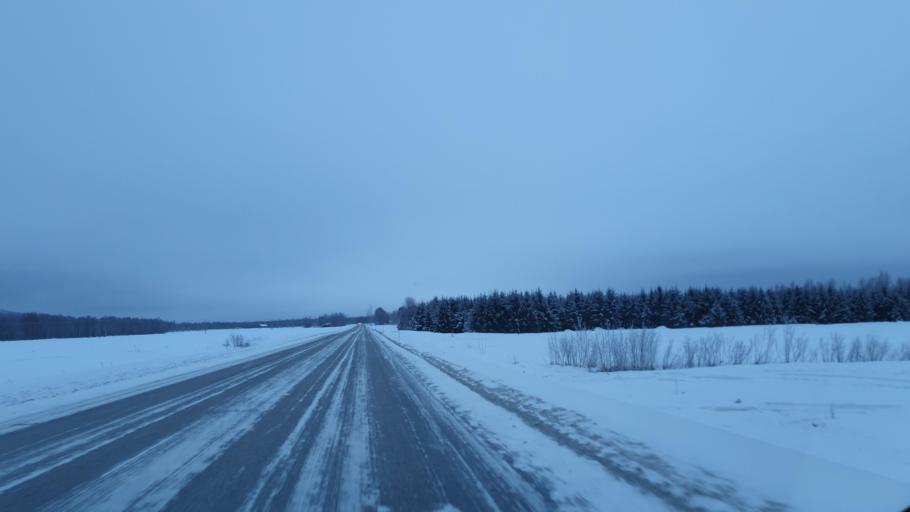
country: SE
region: Norrbotten
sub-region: Overtornea Kommun
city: OEvertornea
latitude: 66.4185
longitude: 23.6662
